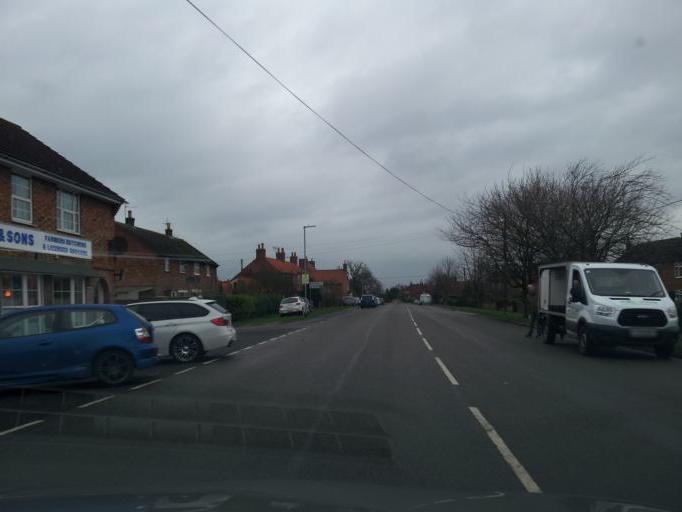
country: GB
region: England
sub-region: Lincolnshire
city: Long Bennington
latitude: 52.9956
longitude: -0.7586
